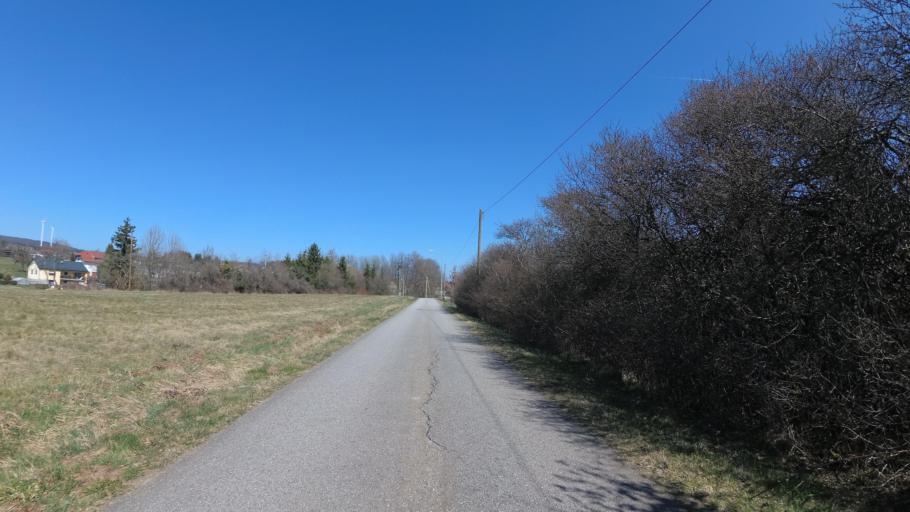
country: DE
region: Rheinland-Pfalz
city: Achtelsbach
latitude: 49.6053
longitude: 7.0540
